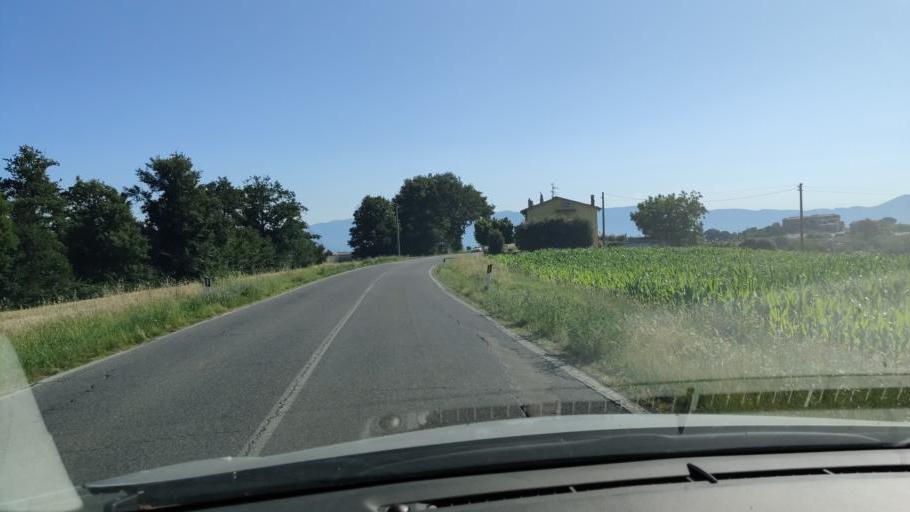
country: IT
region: Umbria
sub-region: Provincia di Terni
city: Avigliano Umbro
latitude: 42.6692
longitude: 12.4421
